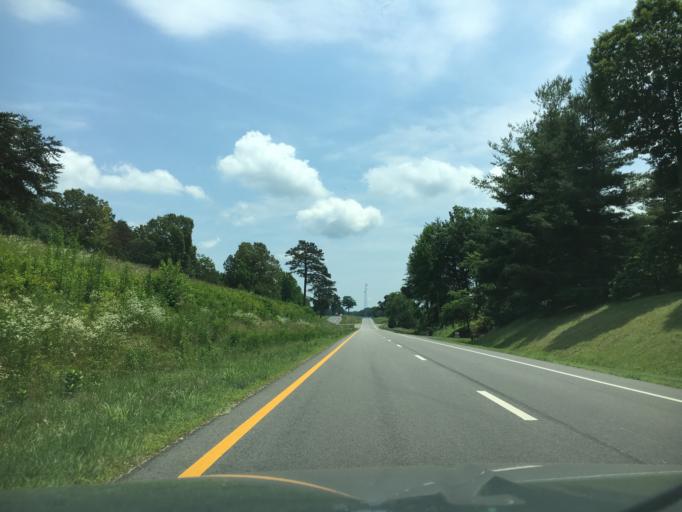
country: US
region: Virginia
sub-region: Buckingham County
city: Buckingham
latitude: 37.5379
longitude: -78.5079
